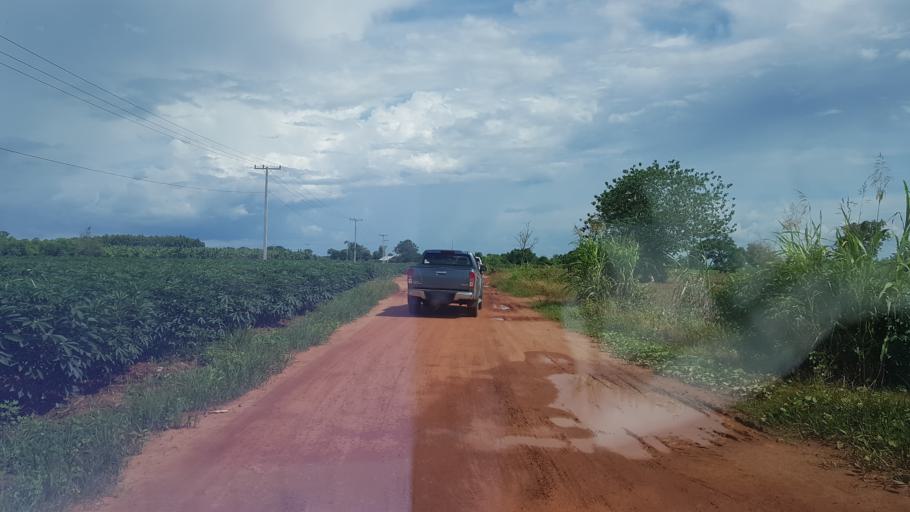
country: LA
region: Vientiane
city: Vientiane
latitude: 18.2288
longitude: 102.5643
